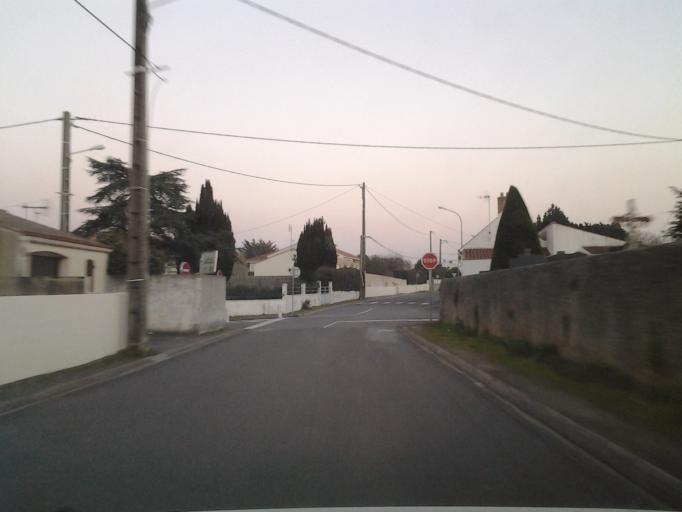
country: FR
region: Pays de la Loire
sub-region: Departement de la Vendee
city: Beauvoir-sur-Mer
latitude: 46.9125
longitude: -2.0409
